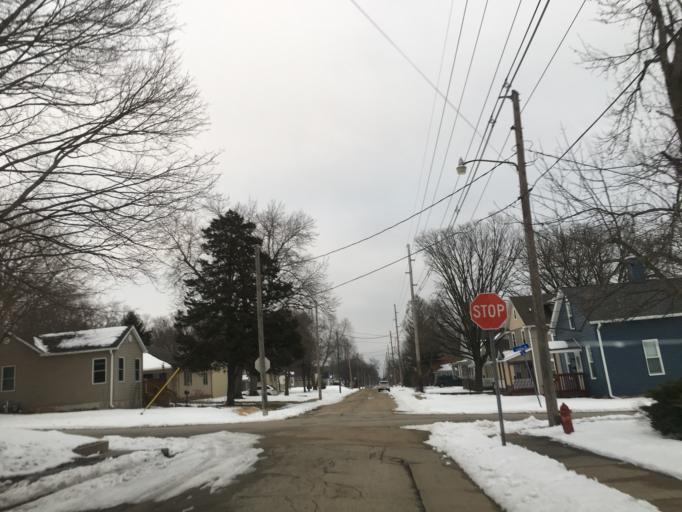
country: US
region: Illinois
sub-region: LaSalle County
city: Peru
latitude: 41.3249
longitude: -89.1347
